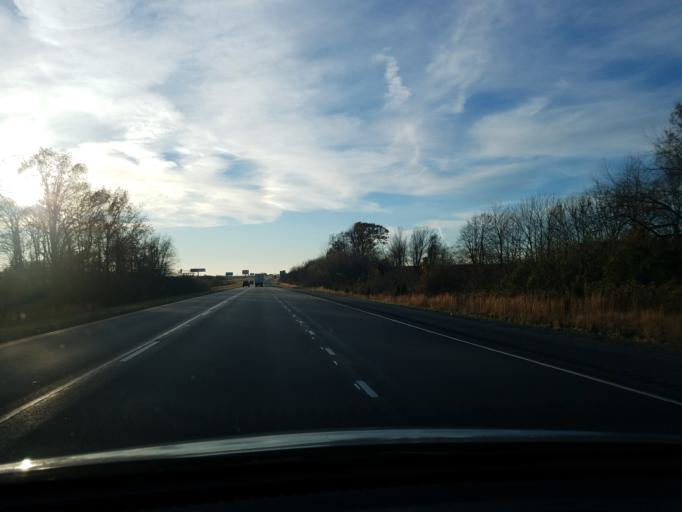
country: US
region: Indiana
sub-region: Spencer County
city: Dale
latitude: 38.1958
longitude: -86.9551
